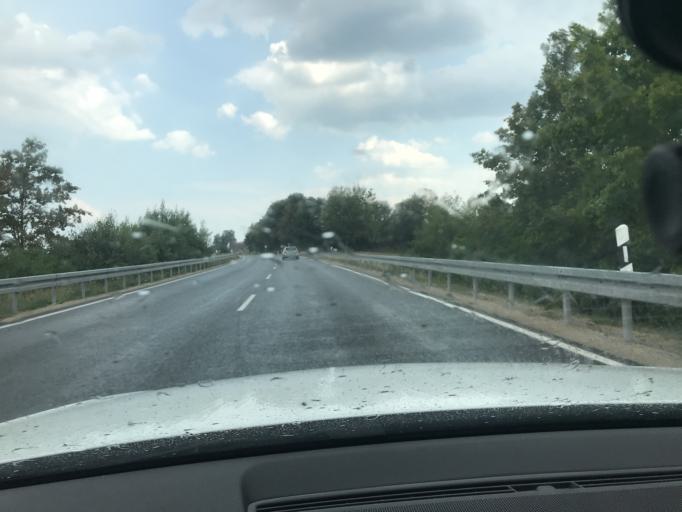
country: DE
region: Bavaria
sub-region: Upper Palatinate
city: Grafenwohr
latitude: 49.7415
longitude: 11.8612
